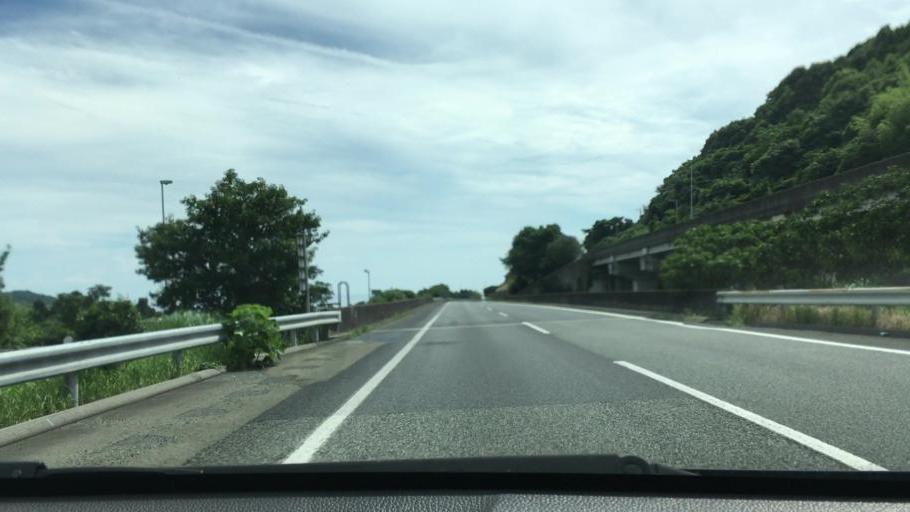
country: JP
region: Yamaguchi
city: Hofu
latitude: 34.0648
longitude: 131.6561
